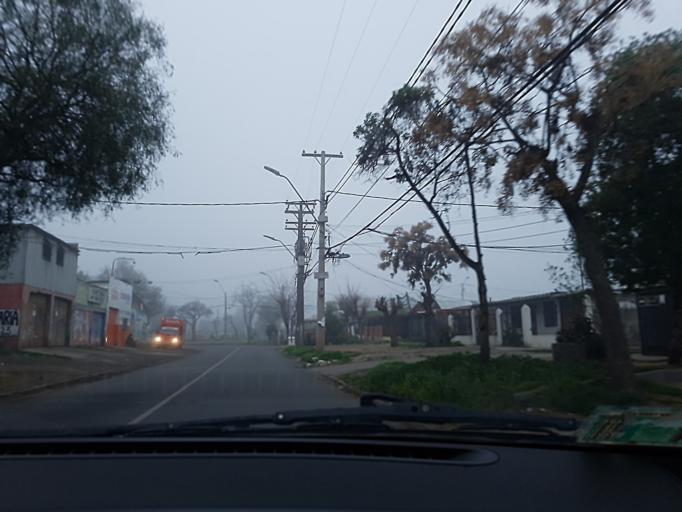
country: CL
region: Santiago Metropolitan
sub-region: Provincia de Santiago
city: Lo Prado
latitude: -33.4744
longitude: -70.7003
